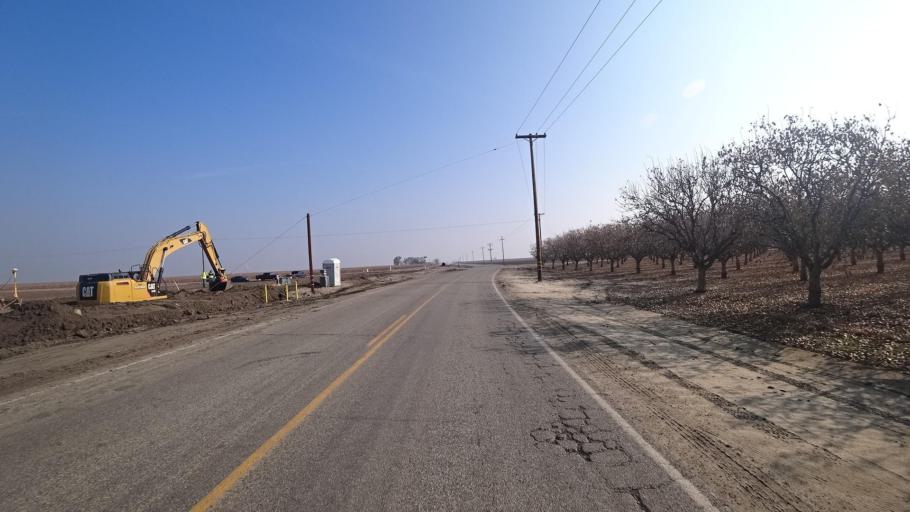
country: US
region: California
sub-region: Kern County
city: Buttonwillow
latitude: 35.3546
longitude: -119.4133
